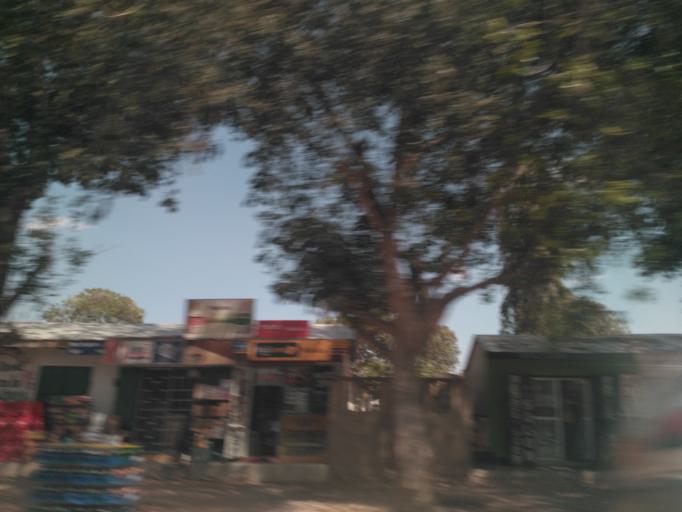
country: TZ
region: Dodoma
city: Dodoma
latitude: -6.1572
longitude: 35.7219
